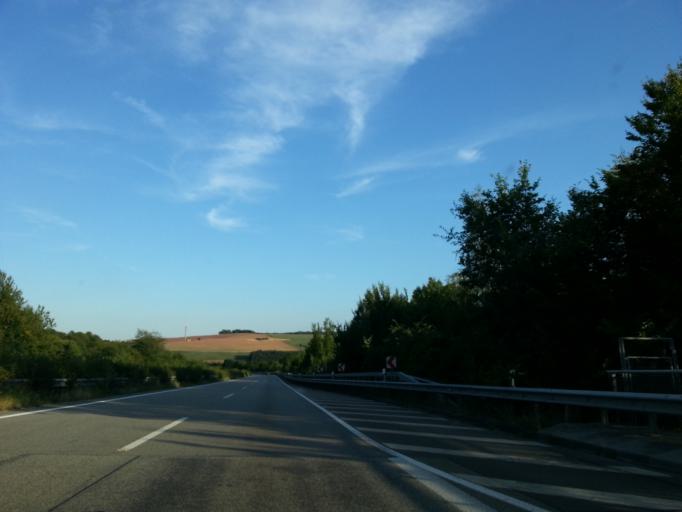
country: DE
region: Rheinland-Pfalz
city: Rehweiler
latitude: 49.4808
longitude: 7.4179
